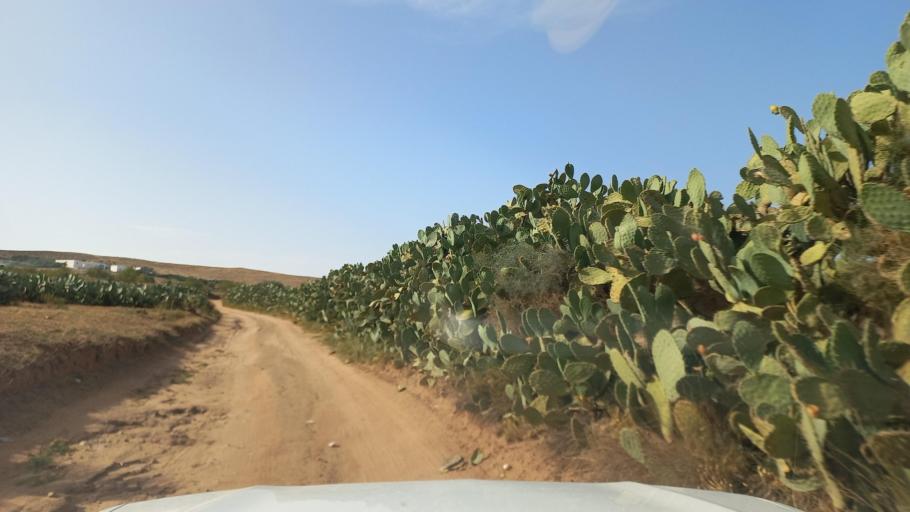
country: TN
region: Al Qasrayn
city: Kasserine
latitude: 35.3612
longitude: 8.8509
